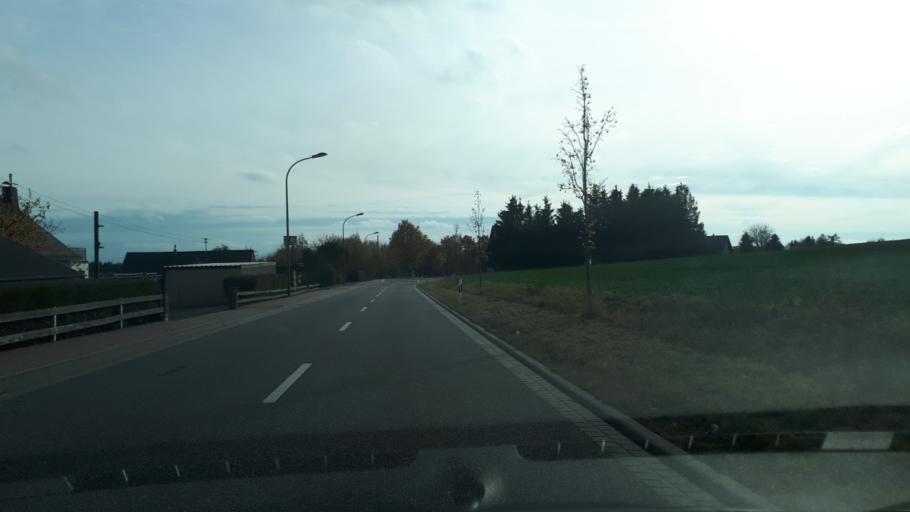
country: DE
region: Rheinland-Pfalz
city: Laubach
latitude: 50.2290
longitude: 7.0729
